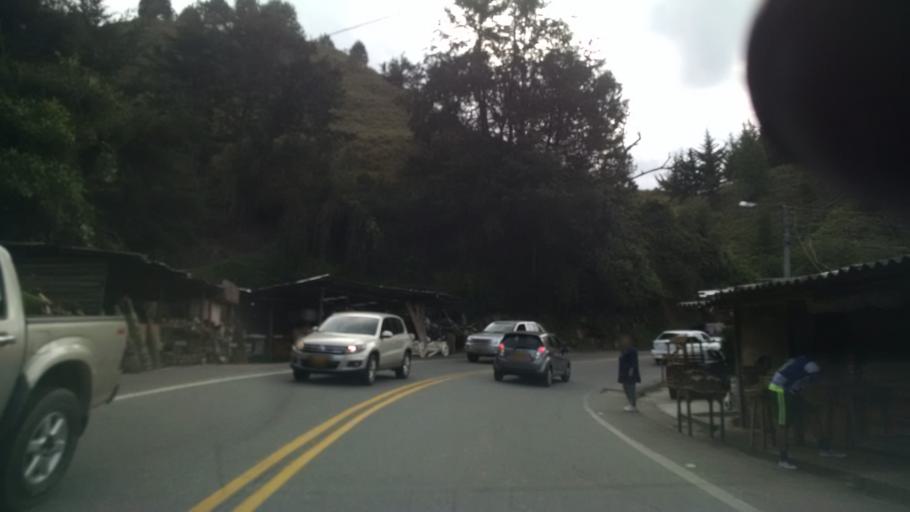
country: CO
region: Antioquia
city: El Retiro
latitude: 6.1299
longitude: -75.5034
